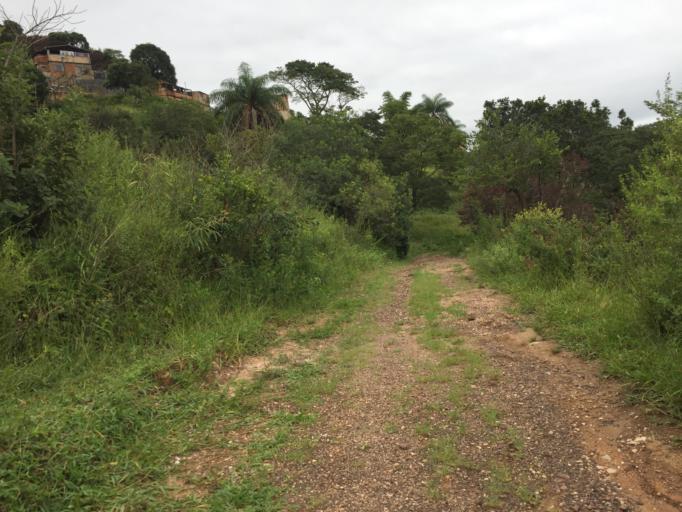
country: BR
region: Minas Gerais
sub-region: Sao Joao Del Rei
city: Sao Joao del Rei
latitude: -21.1279
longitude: -44.2678
